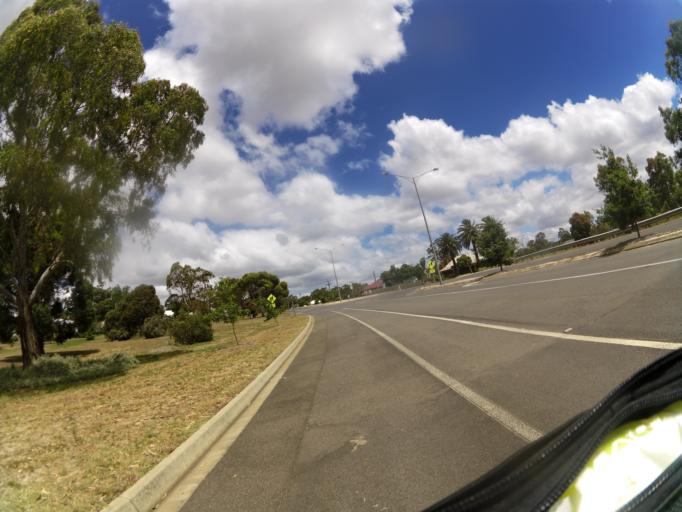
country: AU
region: Victoria
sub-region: Mount Alexander
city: Castlemaine
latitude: -36.9990
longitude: 144.2604
